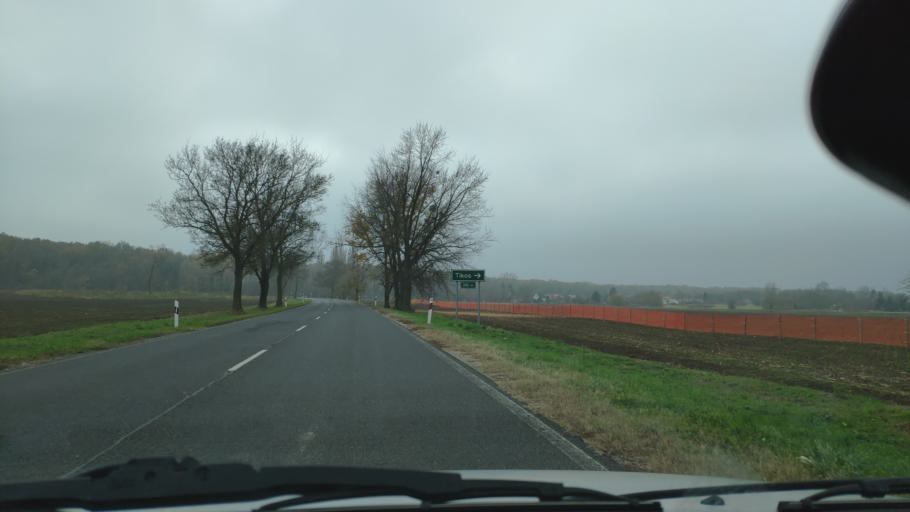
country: HU
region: Somogy
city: Balatonbereny
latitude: 46.6379
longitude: 17.2952
